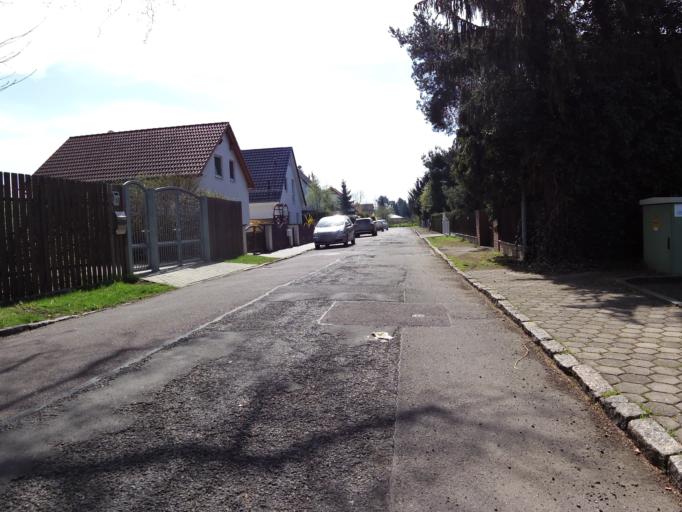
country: DE
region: Saxony
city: Markranstadt
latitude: 51.3171
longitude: 12.2711
